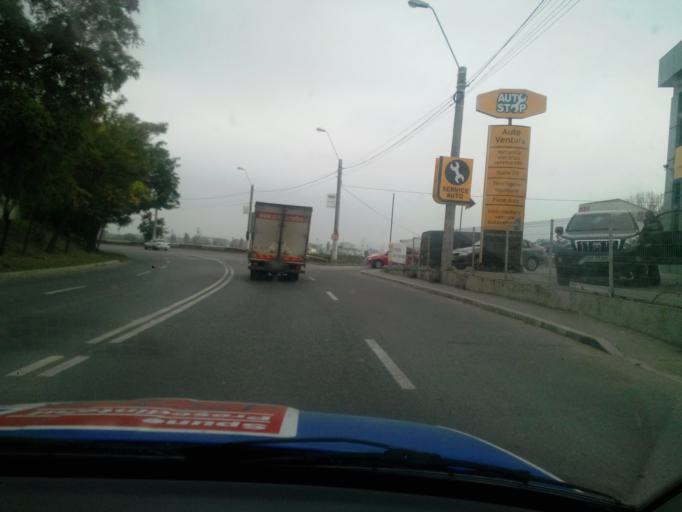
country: RO
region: Braila
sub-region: Municipiul Braila
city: Braila
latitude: 45.2864
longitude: 27.9777
